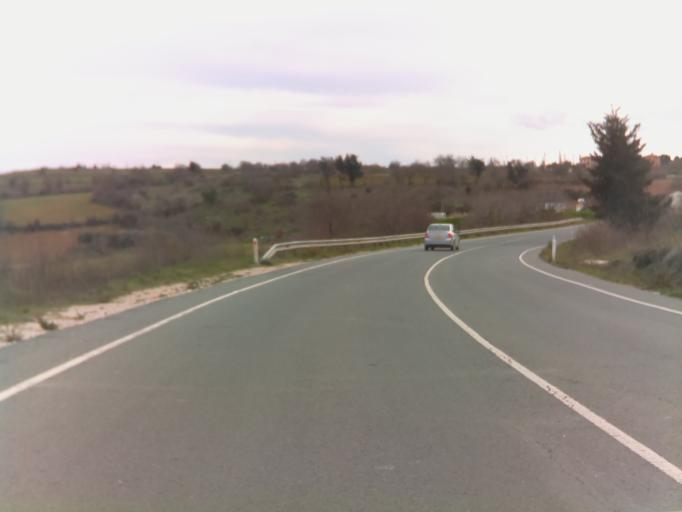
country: CY
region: Pafos
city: Pegeia
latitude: 34.9453
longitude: 32.4123
